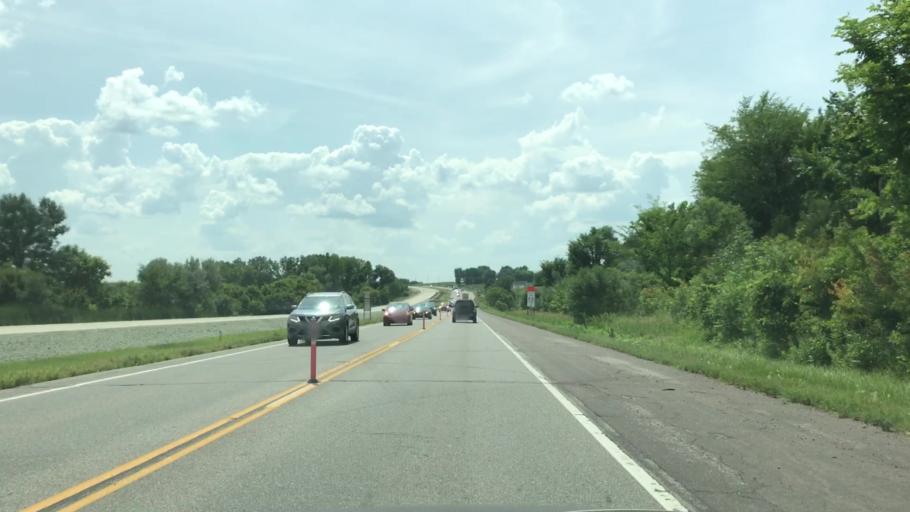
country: US
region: Minnesota
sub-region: Scott County
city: Belle Plaine
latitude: 44.5900
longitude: -93.8228
